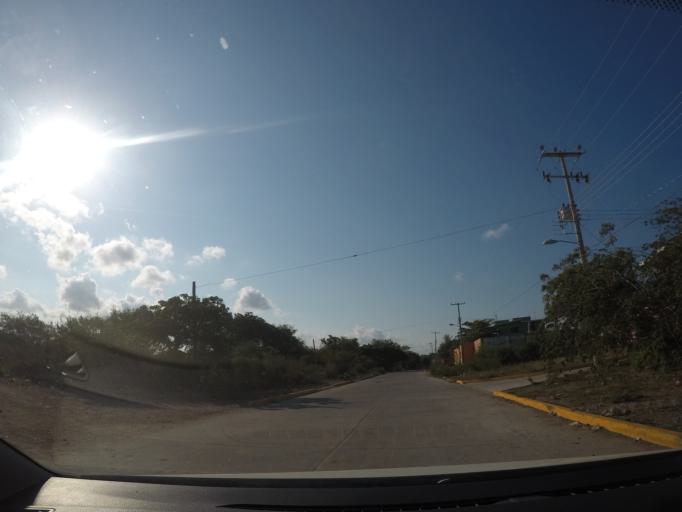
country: MX
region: Oaxaca
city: Juchitan de Zaragoza
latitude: 16.4191
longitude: -95.0226
